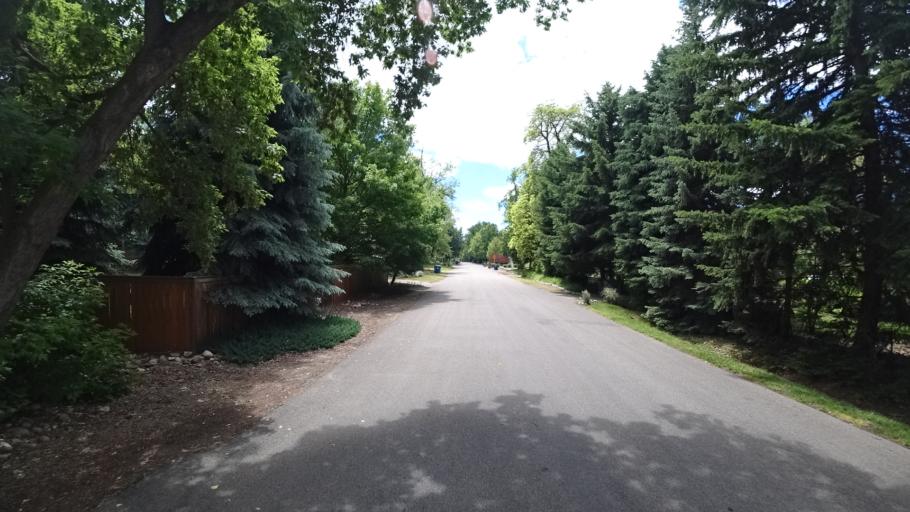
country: US
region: Idaho
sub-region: Ada County
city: Boise
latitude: 43.5856
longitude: -116.1986
